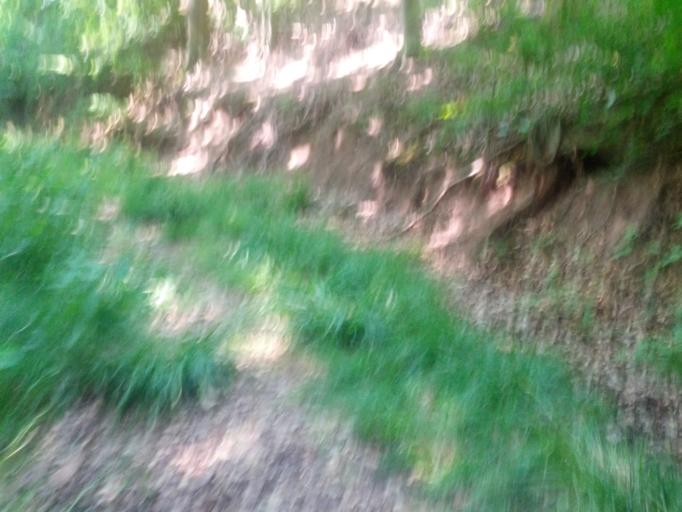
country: DE
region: Thuringia
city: Eisenach
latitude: 50.9733
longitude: 10.2841
